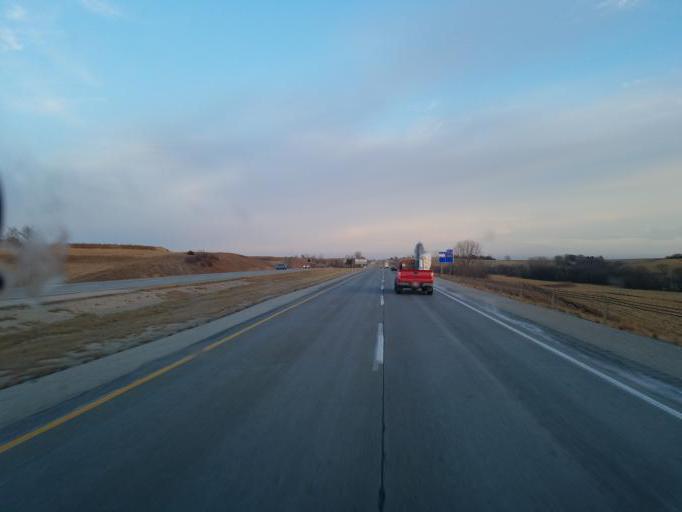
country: US
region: Iowa
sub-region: Pottawattamie County
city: Avoca
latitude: 41.4986
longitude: -95.5687
